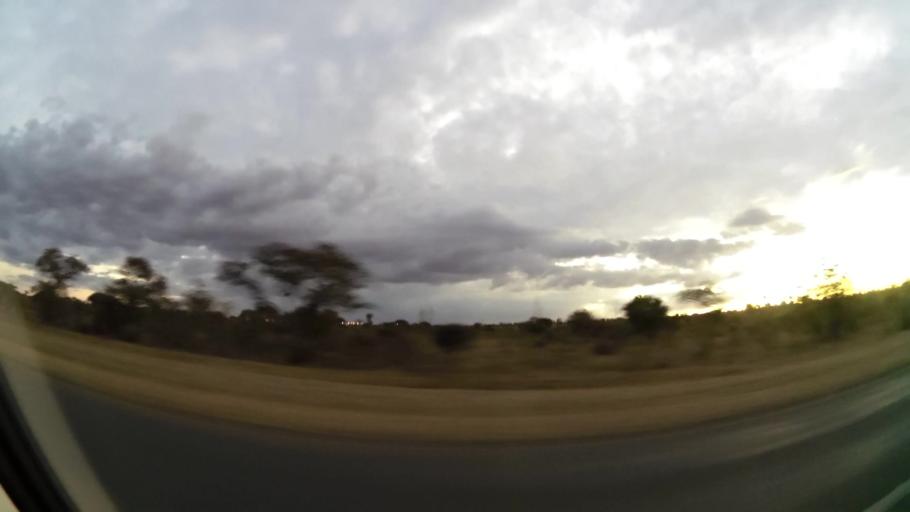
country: ZA
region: Limpopo
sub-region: Capricorn District Municipality
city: Polokwane
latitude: -23.8510
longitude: 29.4287
